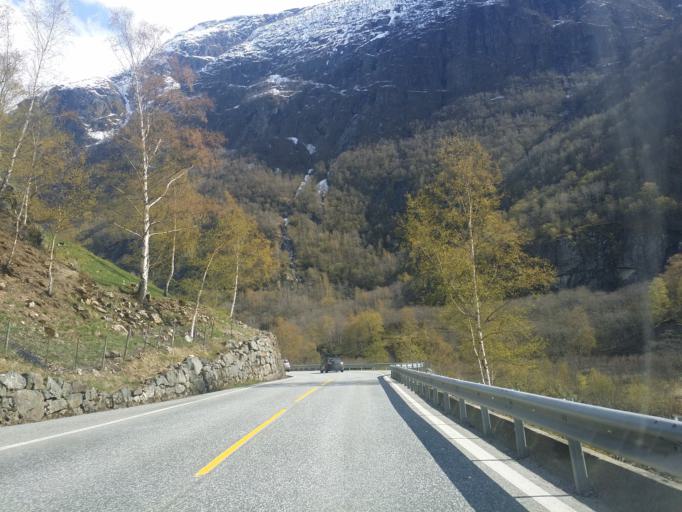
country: NO
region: Hordaland
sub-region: Eidfjord
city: Eidfjord
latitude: 60.4177
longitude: 7.1443
